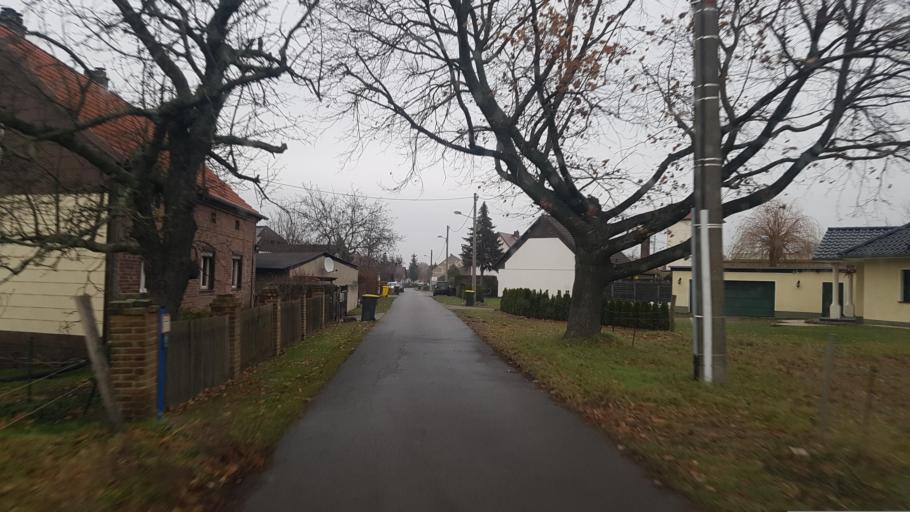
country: DE
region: Brandenburg
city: Drebkau
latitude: 51.6823
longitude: 14.2708
